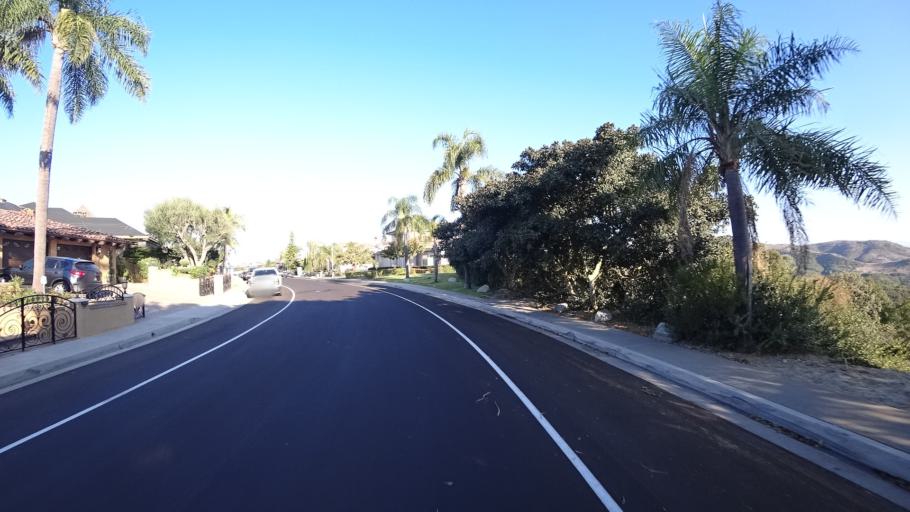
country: US
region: California
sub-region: Orange County
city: San Clemente
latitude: 33.4241
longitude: -117.5927
